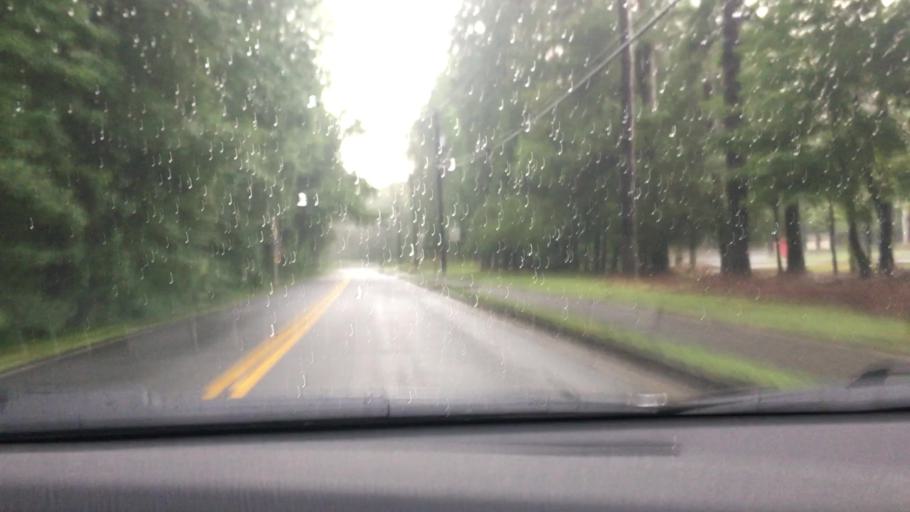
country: US
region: Georgia
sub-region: Fulton County
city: Union City
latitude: 33.6357
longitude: -84.5288
